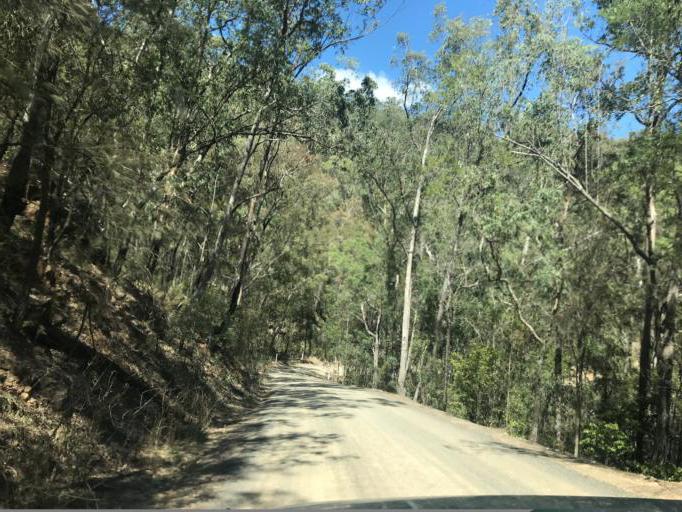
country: AU
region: New South Wales
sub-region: Wyong Shire
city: Little Jilliby
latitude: -33.1607
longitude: 151.0729
